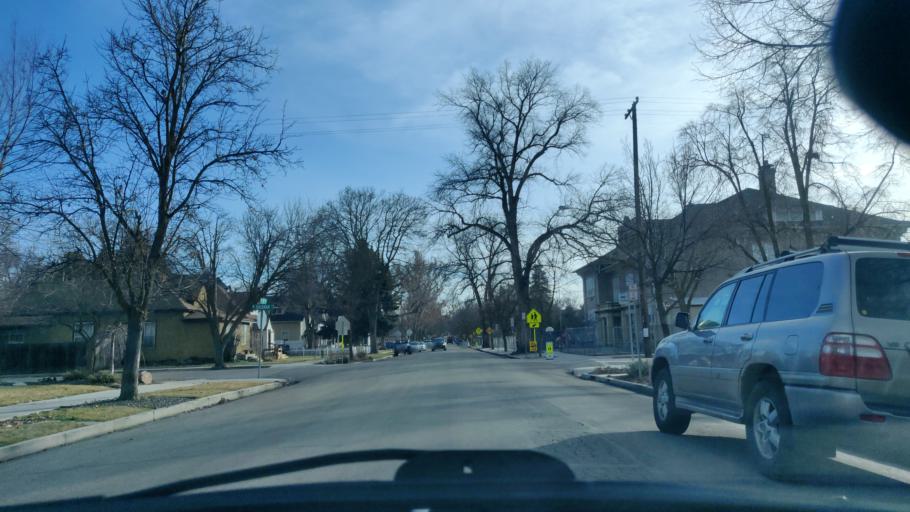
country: US
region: Idaho
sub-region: Ada County
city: Boise
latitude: 43.6287
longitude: -116.1987
